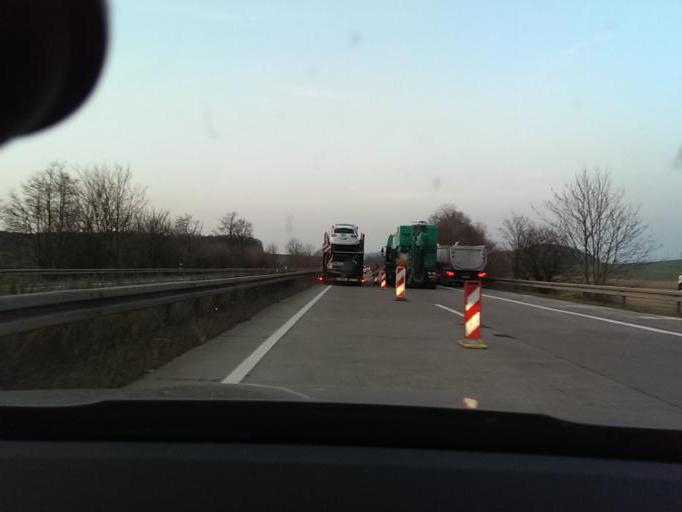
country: DE
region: Lower Saxony
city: Kalefeld
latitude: 51.7581
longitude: 10.0136
